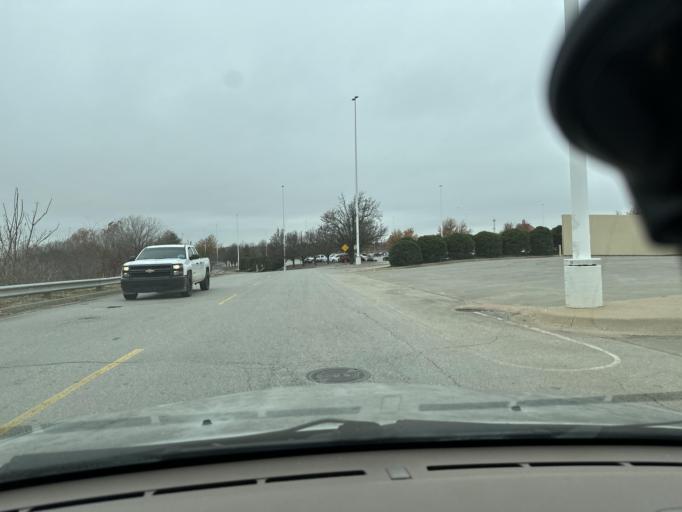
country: US
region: Arkansas
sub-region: Washington County
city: Johnson
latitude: 36.1260
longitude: -94.1481
